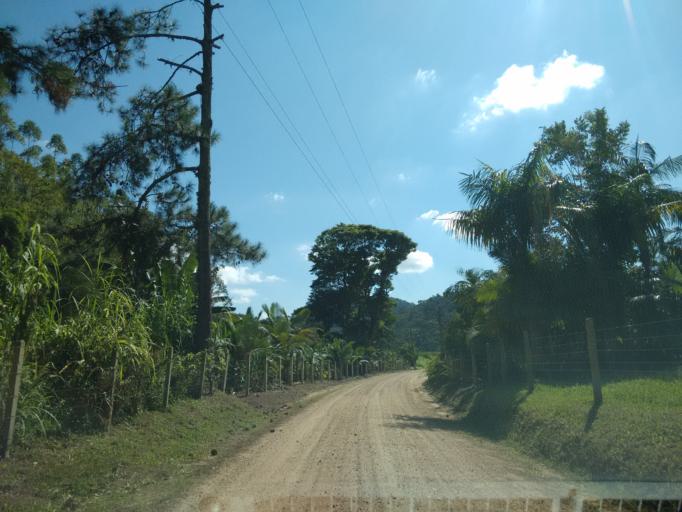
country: BR
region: Santa Catarina
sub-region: Indaial
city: Indaial
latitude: -26.9233
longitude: -49.1883
